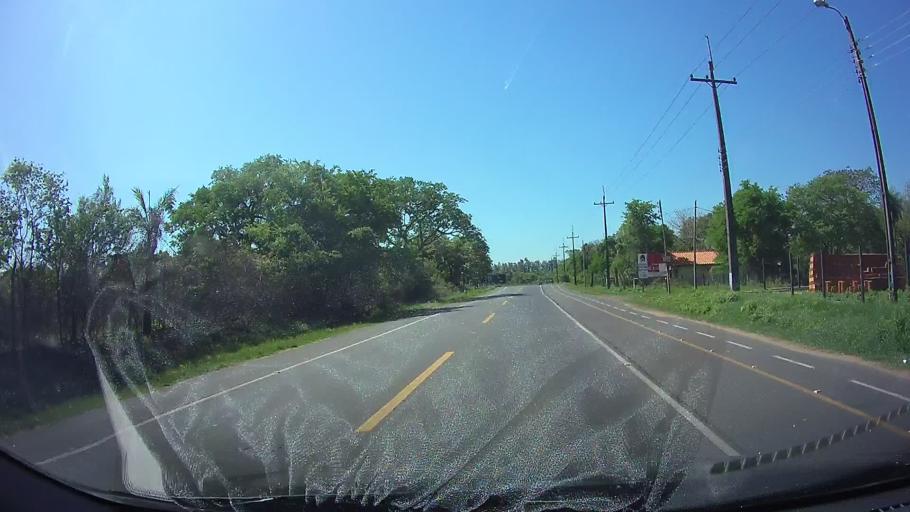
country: PY
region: Central
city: Limpio
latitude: -25.2266
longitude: -57.4181
